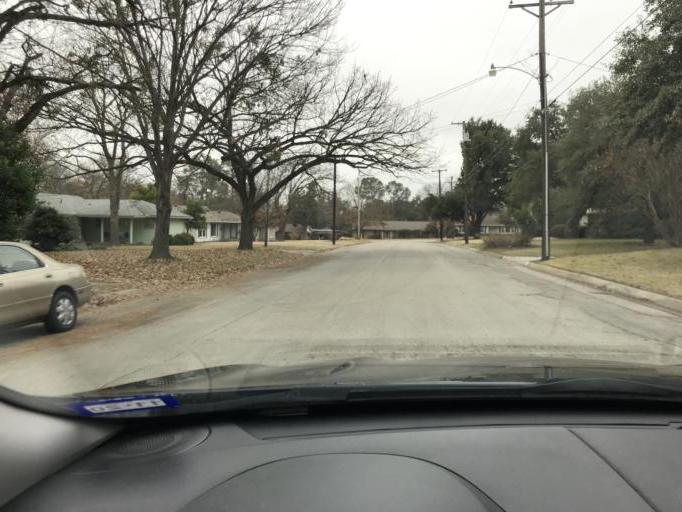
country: US
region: Texas
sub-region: Denton County
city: Denton
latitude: 33.2201
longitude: -97.1570
